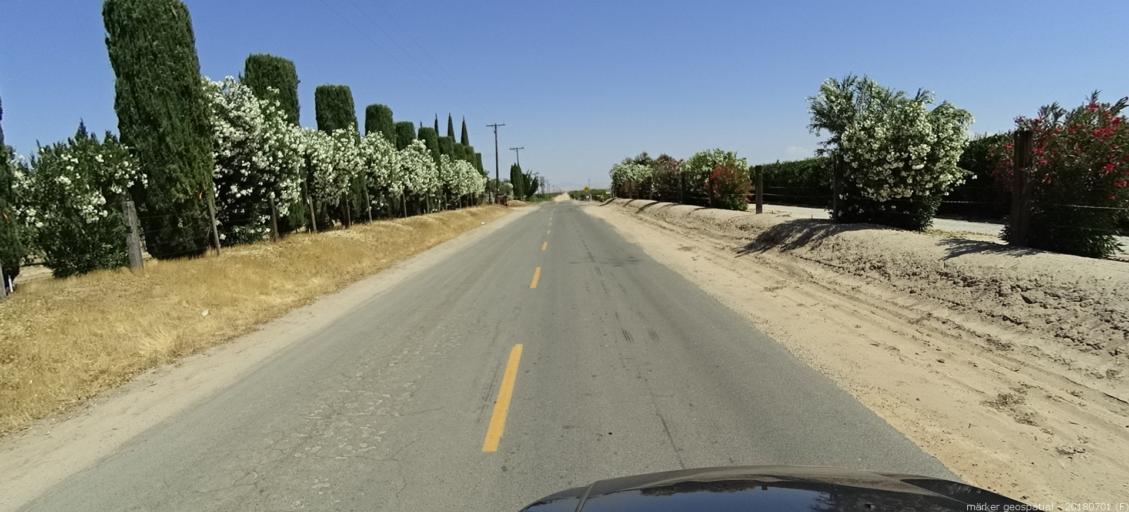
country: US
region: California
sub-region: Madera County
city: Madera Acres
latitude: 37.0721
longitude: -120.0294
